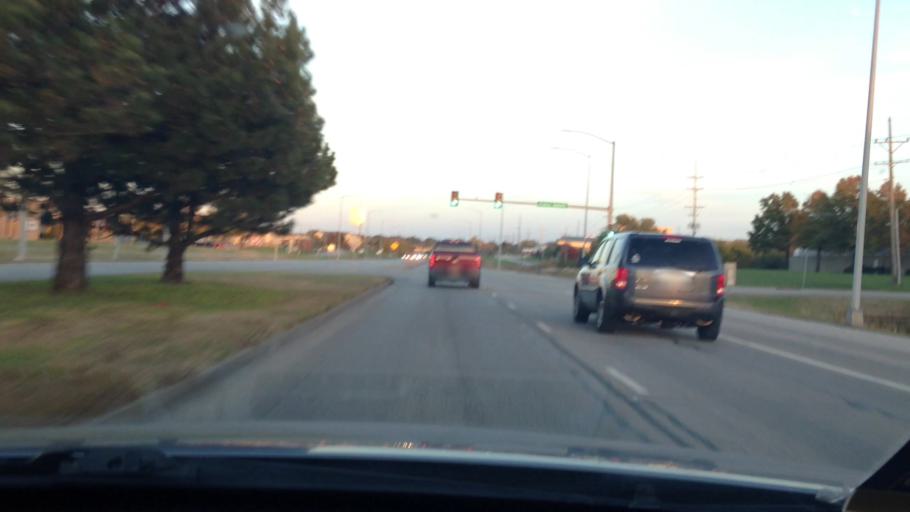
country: US
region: Kansas
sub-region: Johnson County
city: Olathe
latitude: 38.8677
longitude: -94.8139
